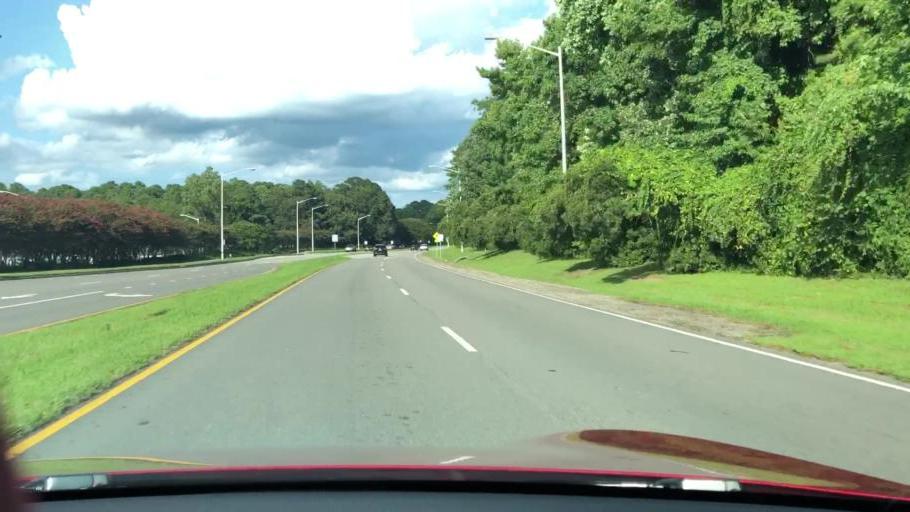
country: US
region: Virginia
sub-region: City of Virginia Beach
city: Virginia Beach
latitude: 36.8209
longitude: -75.9816
